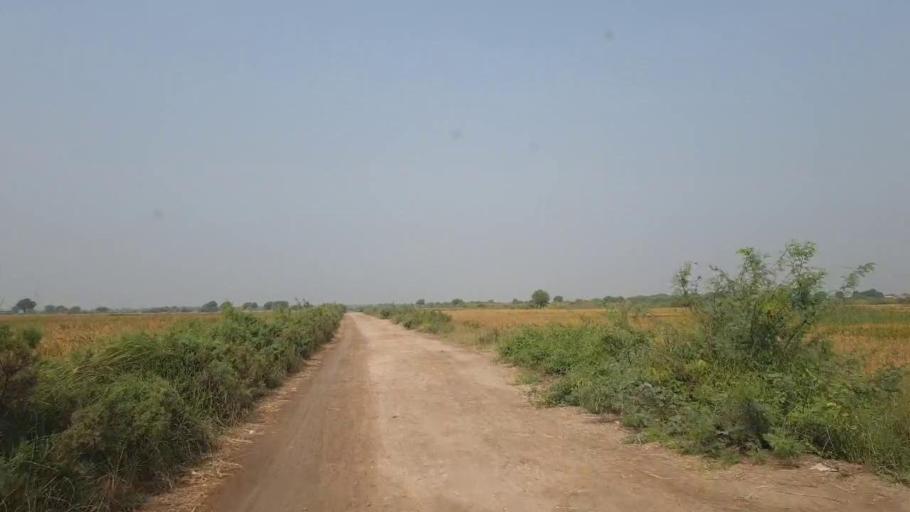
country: PK
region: Sindh
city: Matli
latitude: 25.1653
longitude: 68.7281
